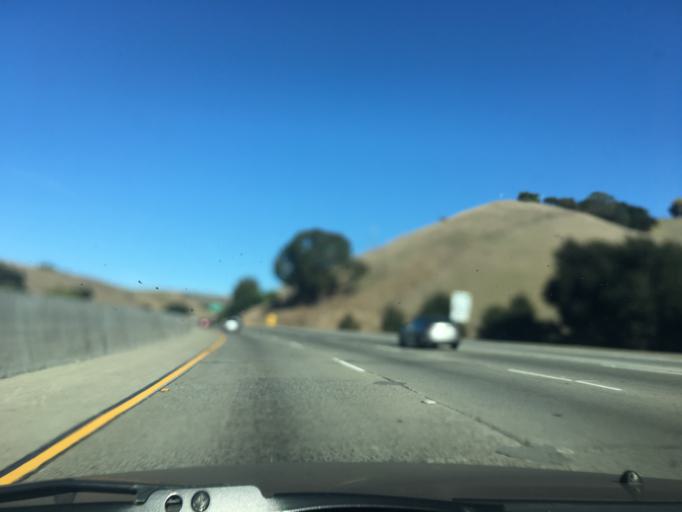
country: US
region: California
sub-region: Alameda County
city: Fremont
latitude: 37.5450
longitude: -121.9202
